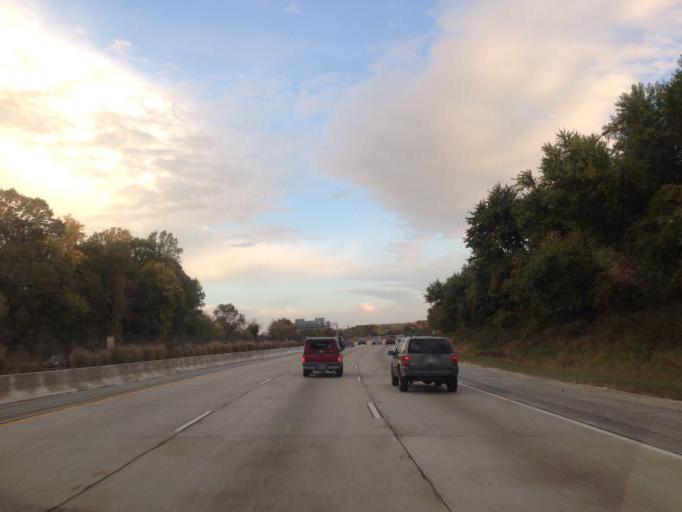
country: US
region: Maryland
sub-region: Baltimore County
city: Garrison
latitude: 39.3919
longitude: -76.7630
